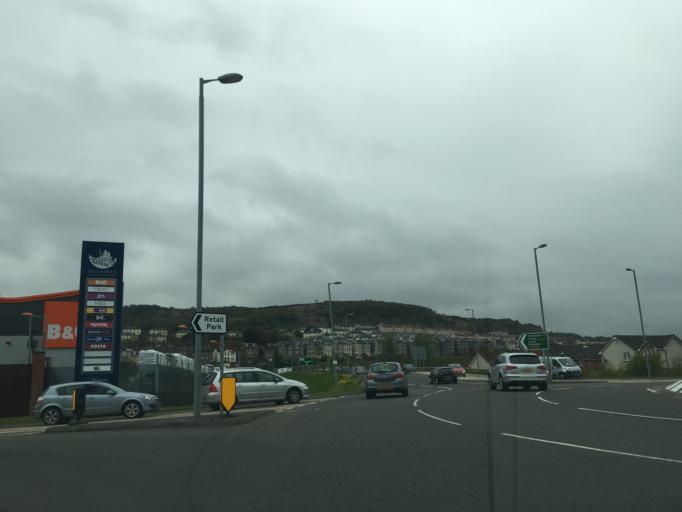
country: GB
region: Scotland
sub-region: Inverclyde
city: Port Glasgow
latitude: 55.9382
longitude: -4.6999
